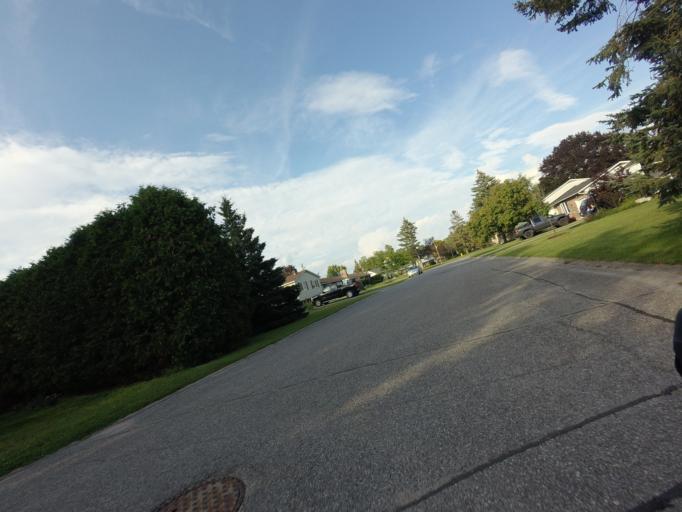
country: CA
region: Ontario
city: Bells Corners
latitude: 45.2844
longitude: -75.7639
